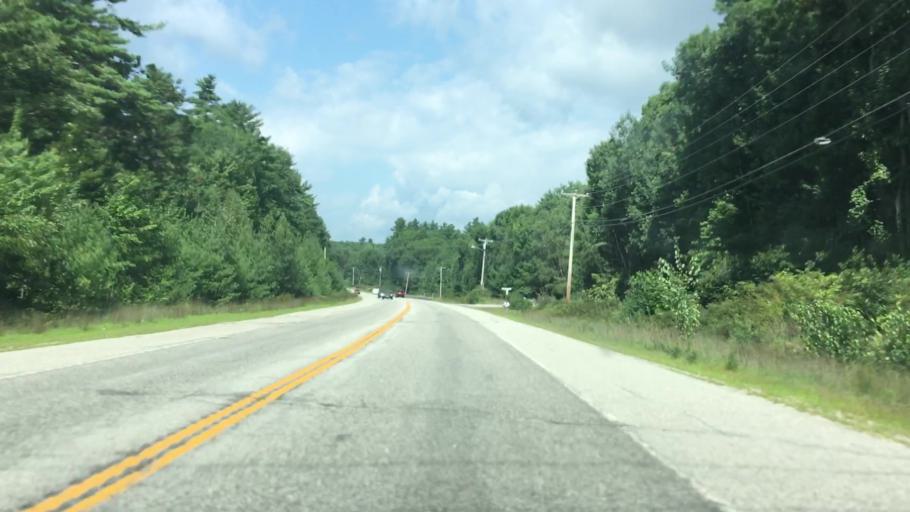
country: US
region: Maine
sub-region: Cumberland County
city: Raymond
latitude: 43.9063
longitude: -70.4880
